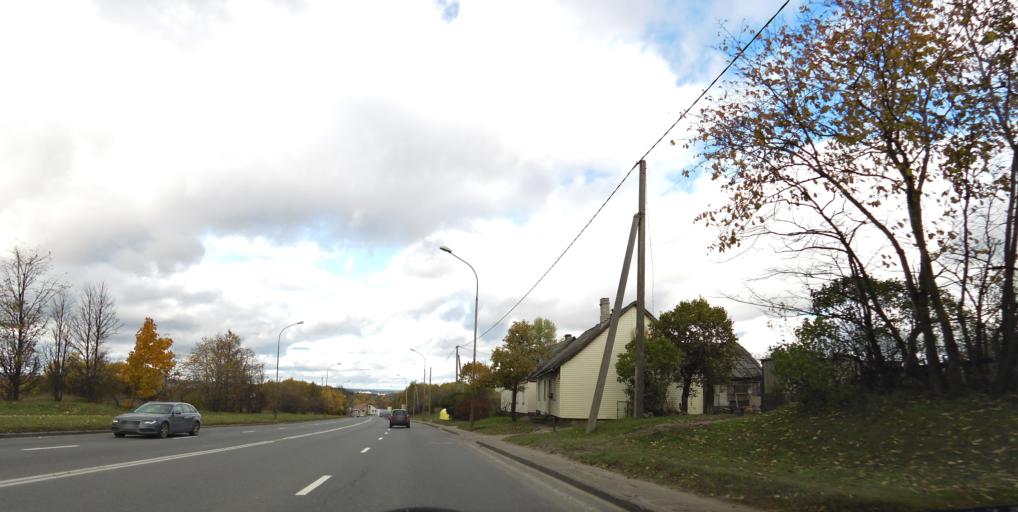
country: LT
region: Vilnius County
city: Rasos
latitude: 54.6572
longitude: 25.3034
